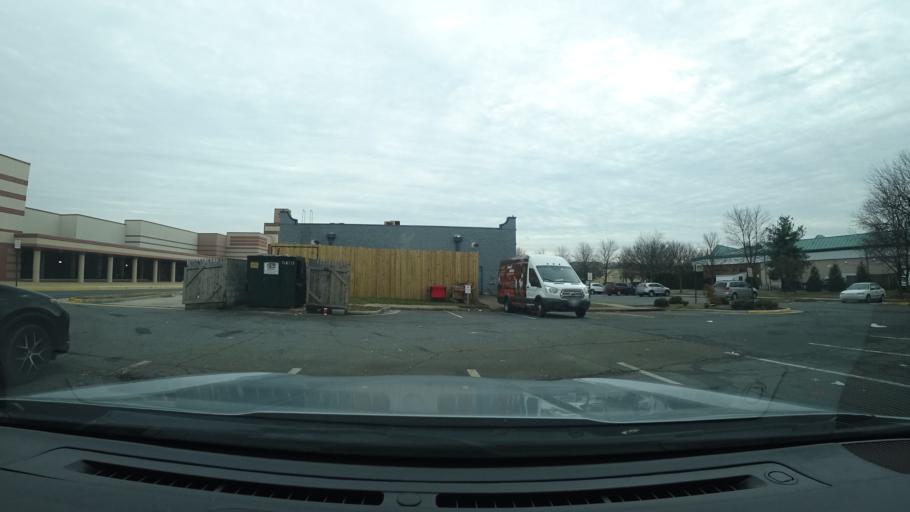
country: US
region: Virginia
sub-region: Loudoun County
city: Countryside
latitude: 39.0374
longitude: -77.4099
